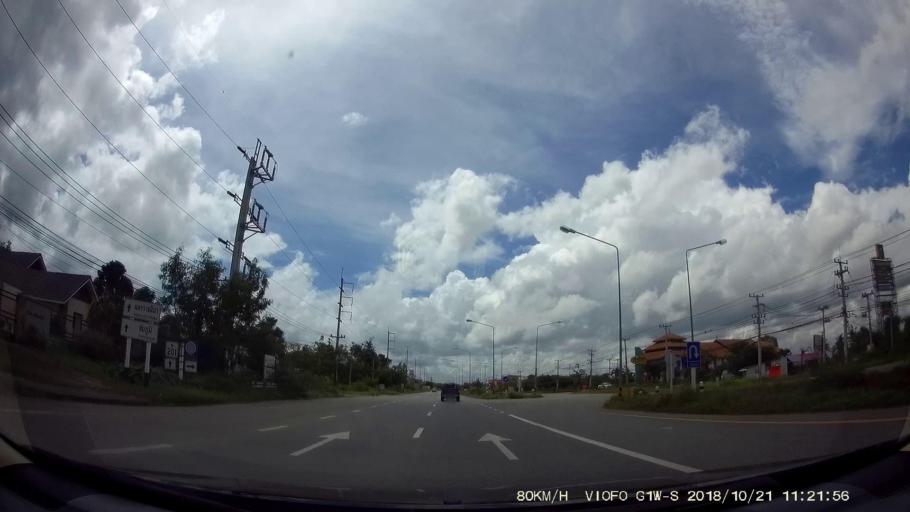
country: TH
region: Chaiyaphum
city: Chaiyaphum
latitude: 15.8412
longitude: 102.0621
